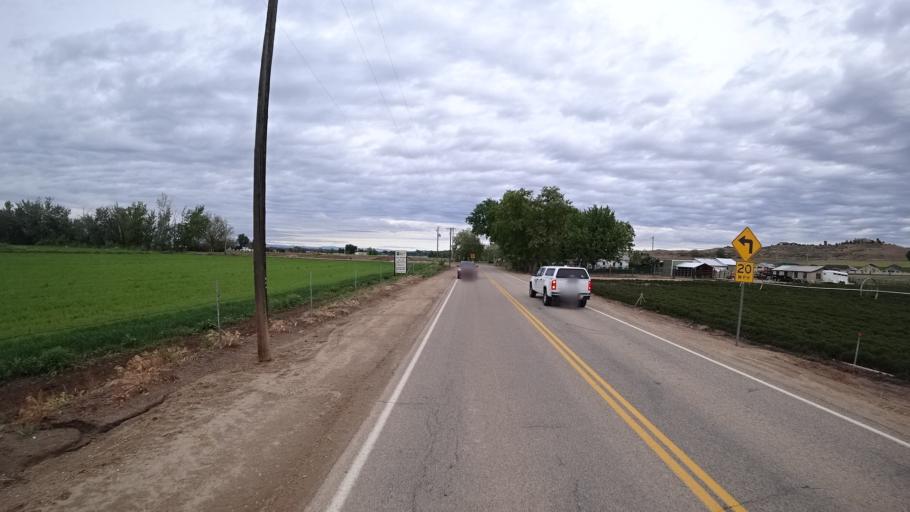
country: US
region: Idaho
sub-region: Ada County
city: Star
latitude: 43.7212
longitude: -116.4819
